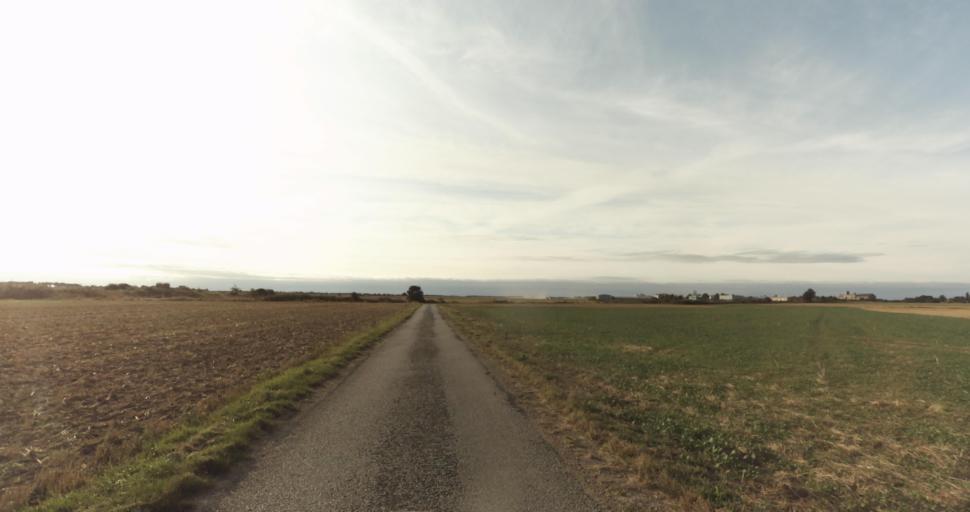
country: FR
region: Haute-Normandie
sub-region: Departement de l'Eure
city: Marcilly-sur-Eure
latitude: 48.8889
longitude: 1.2748
